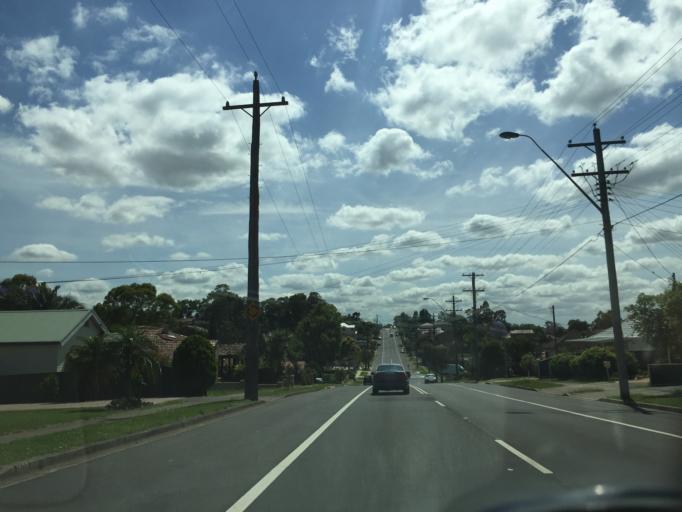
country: AU
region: New South Wales
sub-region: Holroyd
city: Girraween
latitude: -33.7894
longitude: 150.9397
